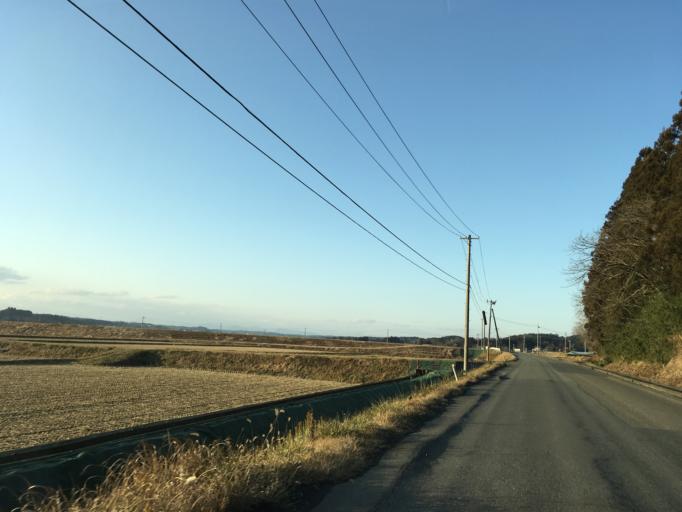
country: JP
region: Iwate
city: Ichinoseki
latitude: 38.8100
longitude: 141.2150
